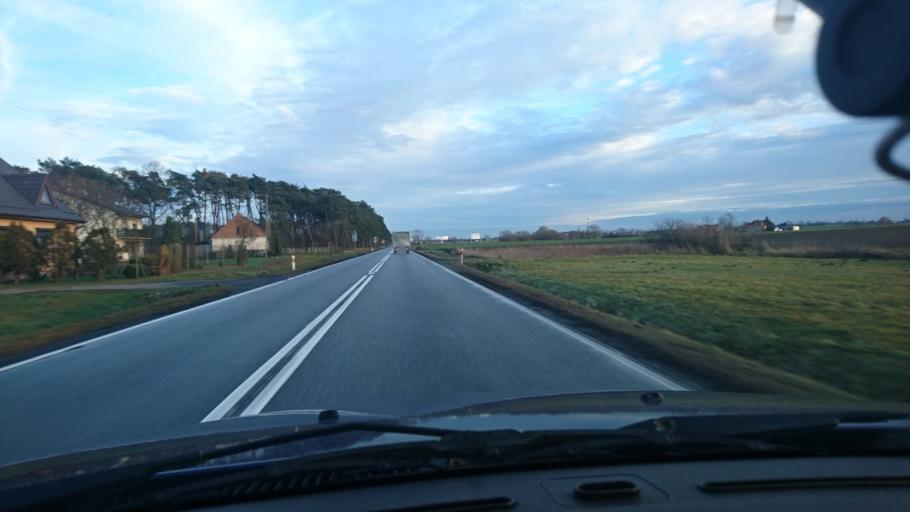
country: PL
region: Greater Poland Voivodeship
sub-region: Powiat kepinski
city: Leka Opatowska
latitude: 51.2230
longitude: 18.1185
